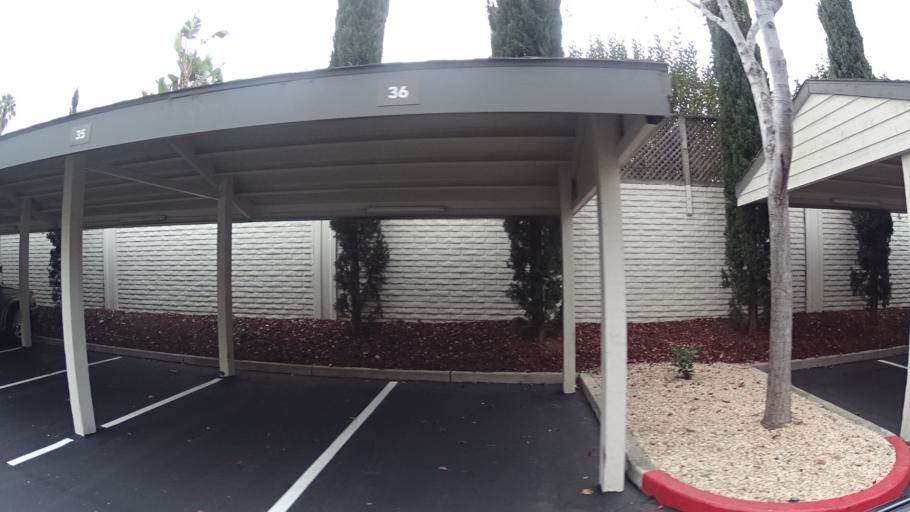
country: US
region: California
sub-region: Santa Clara County
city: Sunnyvale
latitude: 37.3701
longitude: -122.0164
